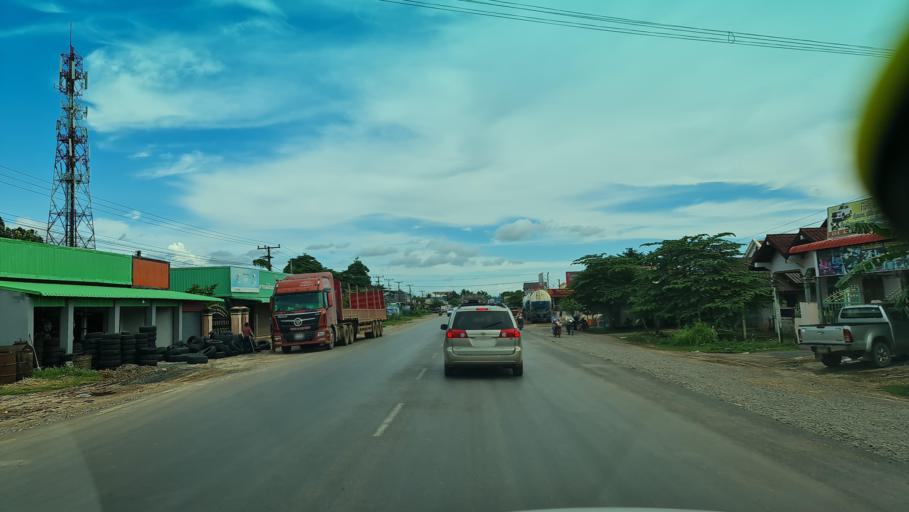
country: TH
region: Nakhon Phanom
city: Ban Phaeng
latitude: 18.1022
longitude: 104.2843
